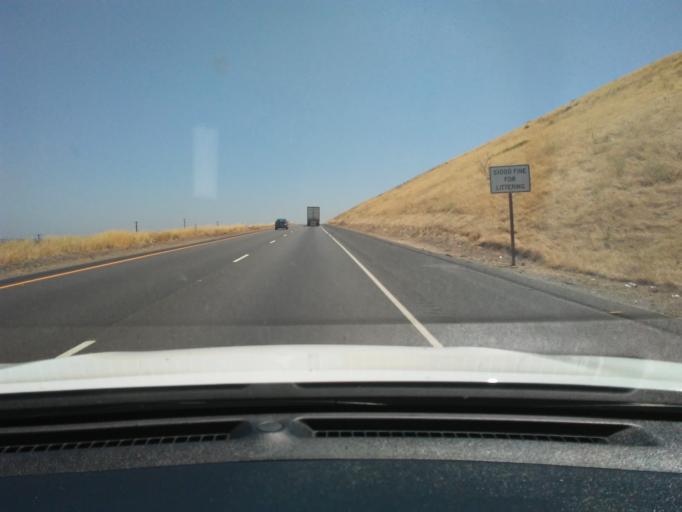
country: US
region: California
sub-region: Stanislaus County
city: Patterson
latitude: 37.4586
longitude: -121.1767
